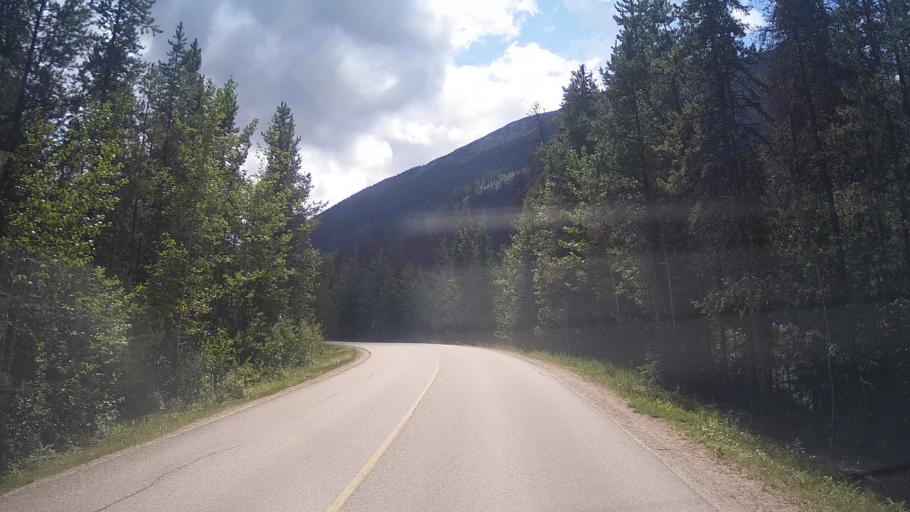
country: CA
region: Alberta
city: Jasper Park Lodge
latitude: 52.8551
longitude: -118.1034
